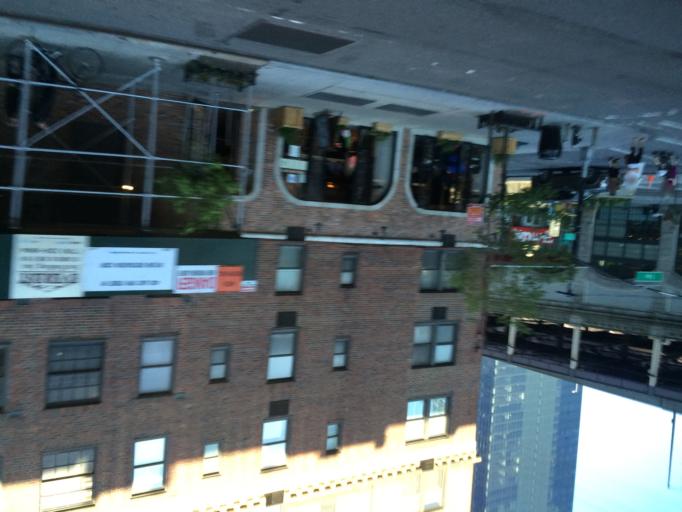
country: US
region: New York
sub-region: Queens County
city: Long Island City
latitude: 40.7595
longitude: -73.9621
